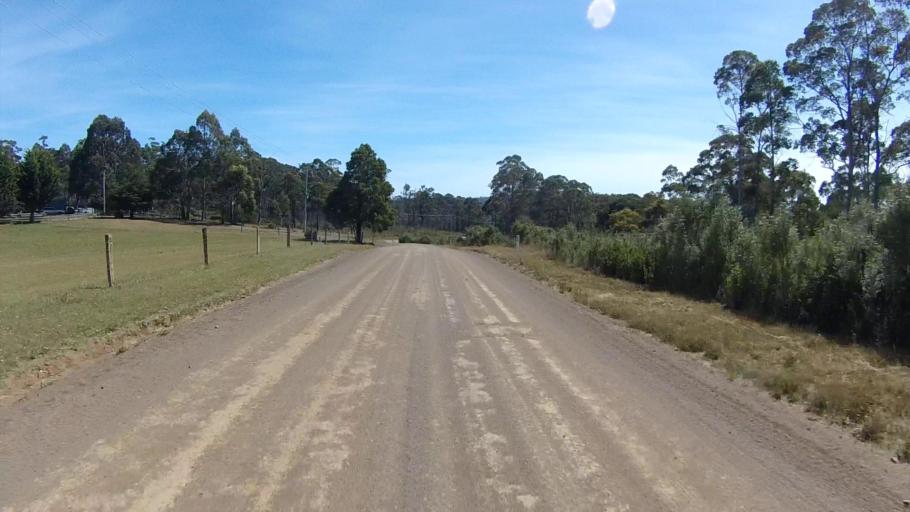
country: AU
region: Tasmania
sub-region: Sorell
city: Sorell
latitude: -42.7304
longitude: 147.7390
